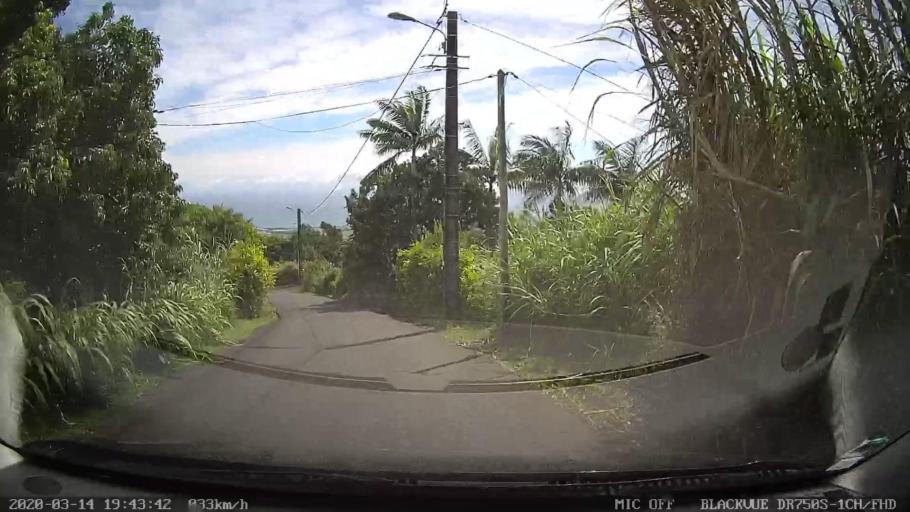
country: RE
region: Reunion
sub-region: Reunion
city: Sainte-Marie
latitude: -20.9478
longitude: 55.5284
